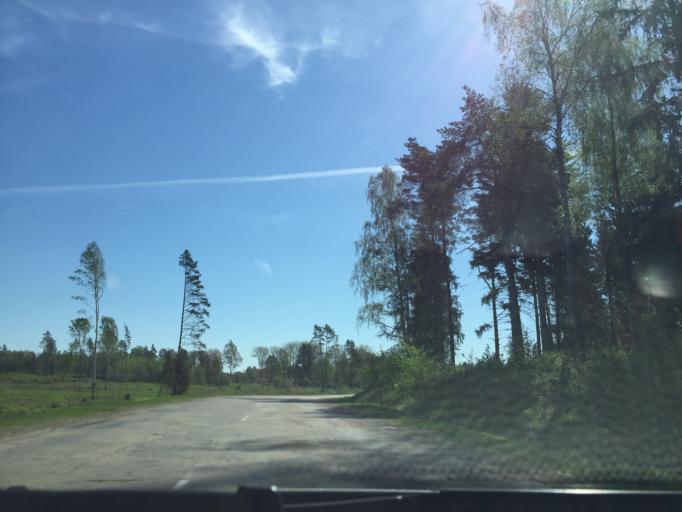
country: LV
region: Ropazu
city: Ropazi
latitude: 57.0081
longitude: 24.5678
